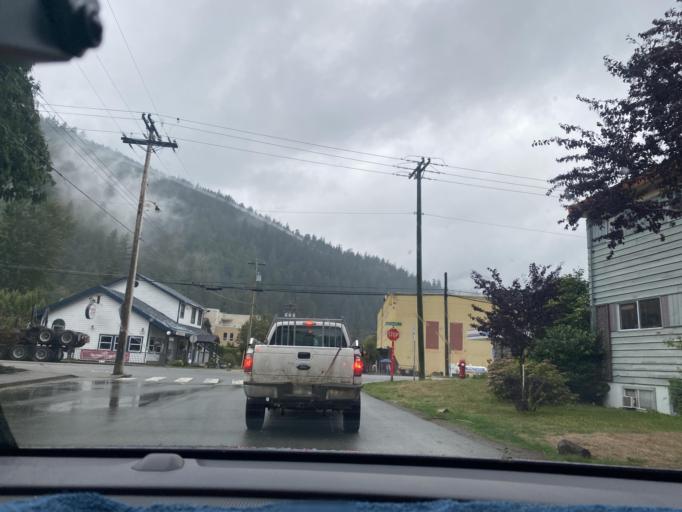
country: CA
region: British Columbia
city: Agassiz
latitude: 49.3018
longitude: -121.7848
